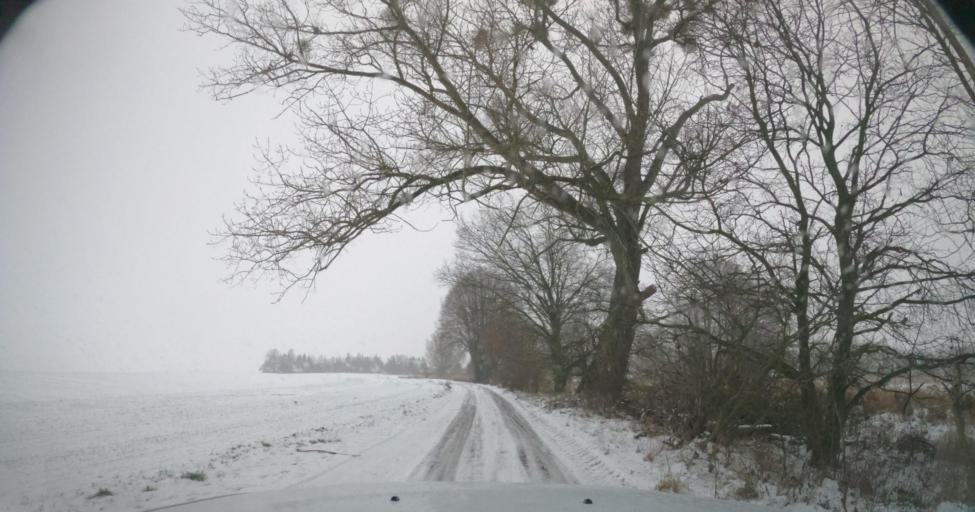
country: PL
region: West Pomeranian Voivodeship
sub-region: Powiat kamienski
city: Golczewo
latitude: 53.7861
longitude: 14.9551
